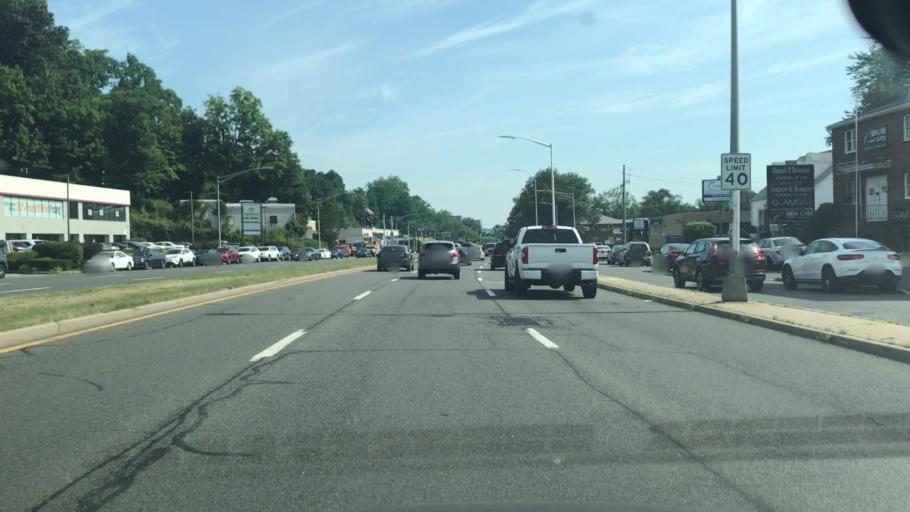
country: US
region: New York
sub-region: Westchester County
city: Tuckahoe
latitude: 40.9718
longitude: -73.8352
